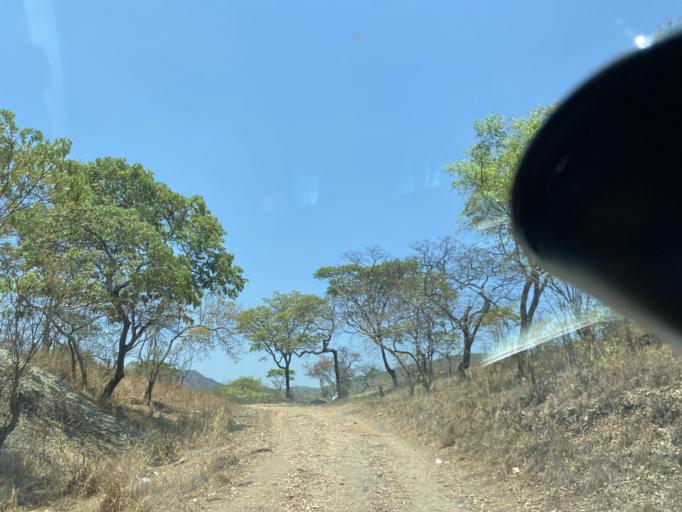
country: ZM
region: Lusaka
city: Kafue
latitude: -15.8060
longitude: 28.4287
